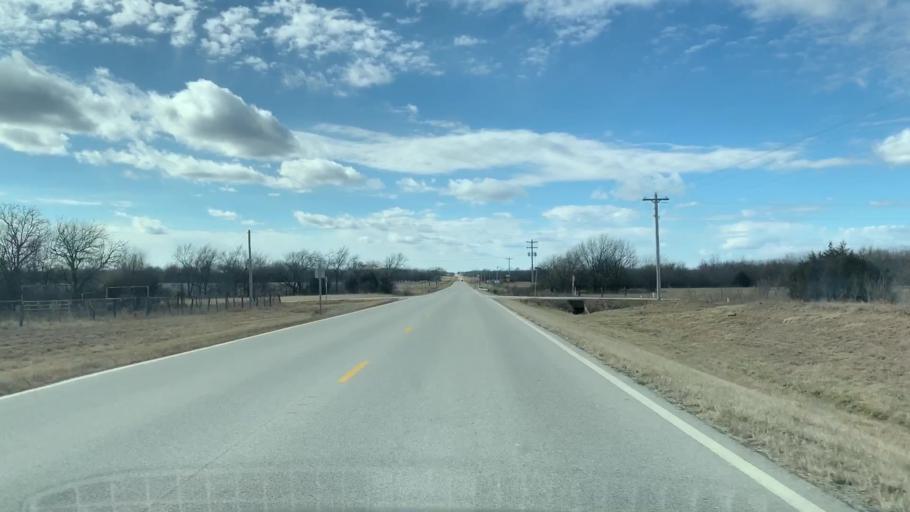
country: US
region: Kansas
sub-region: Neosho County
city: Erie
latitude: 37.5292
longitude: -95.3969
